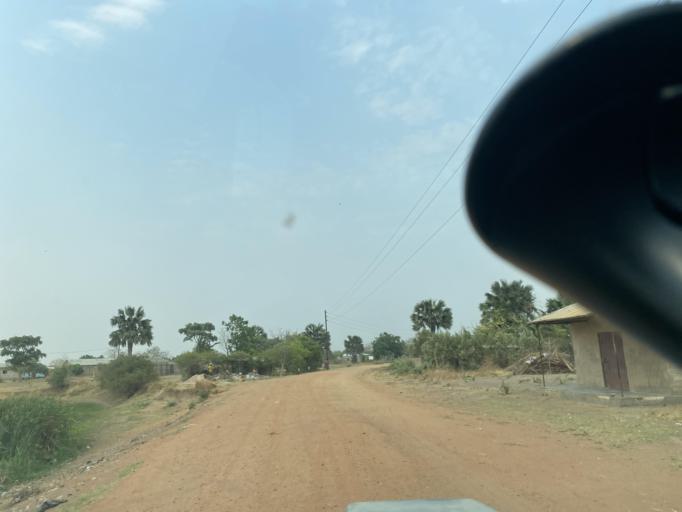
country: ZM
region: Lusaka
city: Kafue
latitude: -15.6715
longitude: 28.0182
